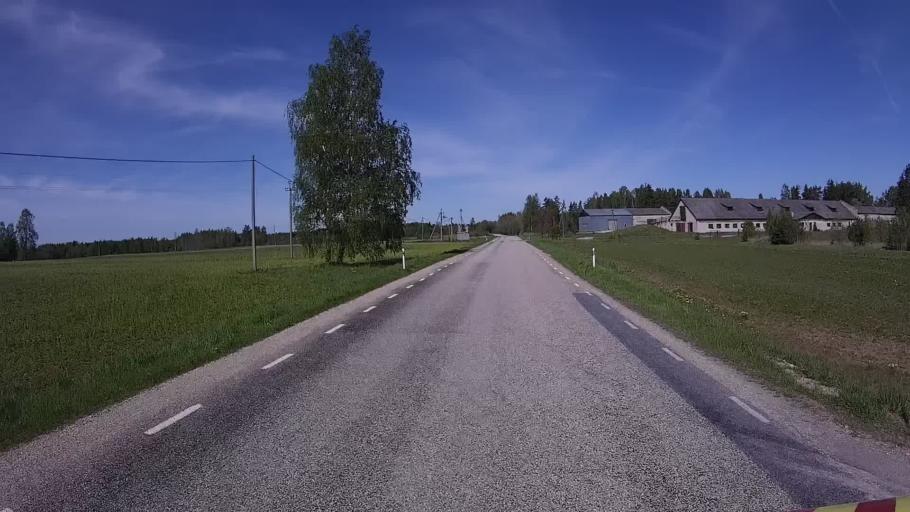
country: EE
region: Polvamaa
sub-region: Raepina vald
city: Rapina
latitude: 57.9667
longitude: 27.5337
